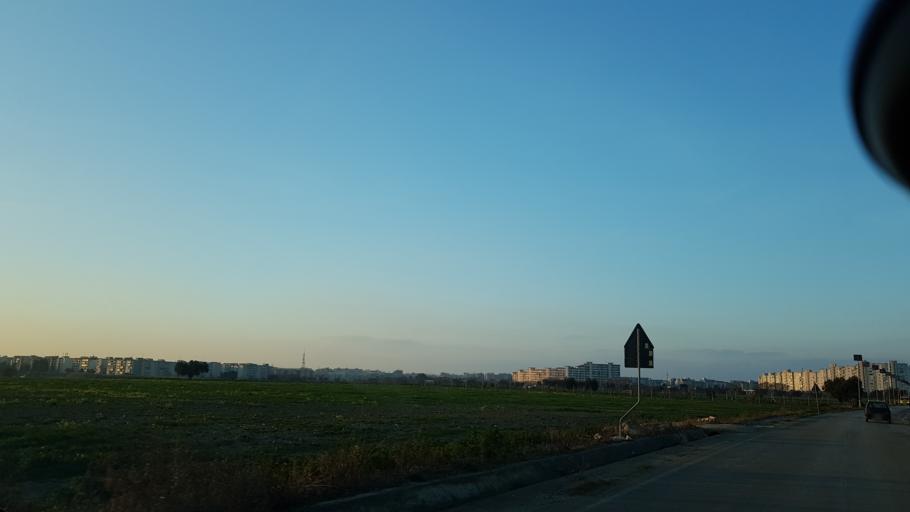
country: IT
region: Apulia
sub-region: Provincia di Brindisi
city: La Rosa
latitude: 40.6120
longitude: 17.9447
